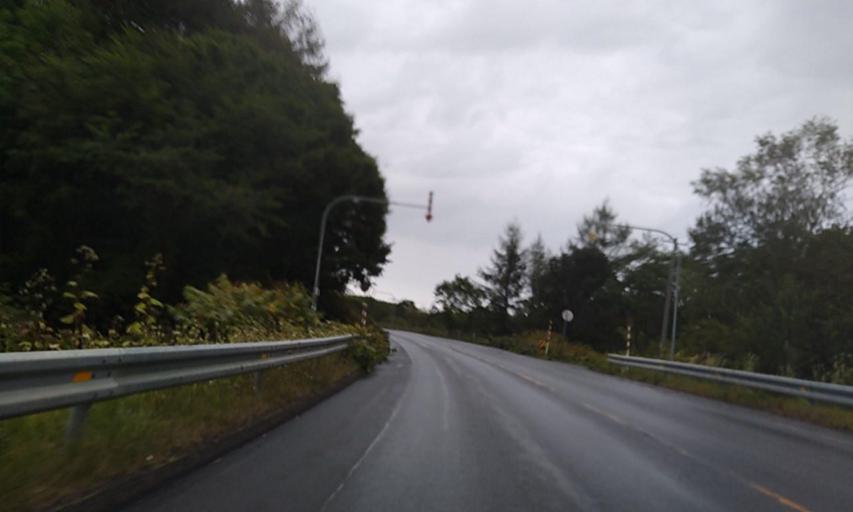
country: JP
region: Hokkaido
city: Mombetsu
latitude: 44.4876
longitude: 143.0751
